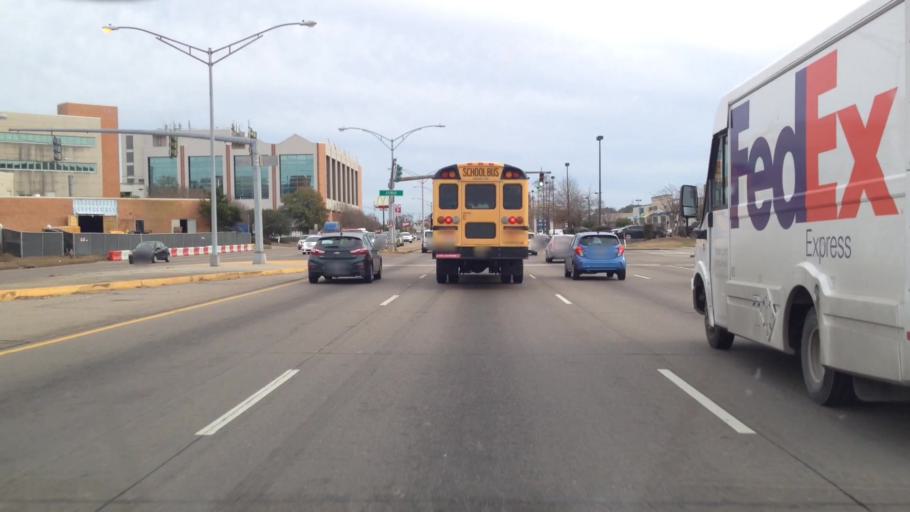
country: US
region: Louisiana
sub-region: Jefferson Parish
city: Elmwood
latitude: 29.9646
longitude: -90.1855
